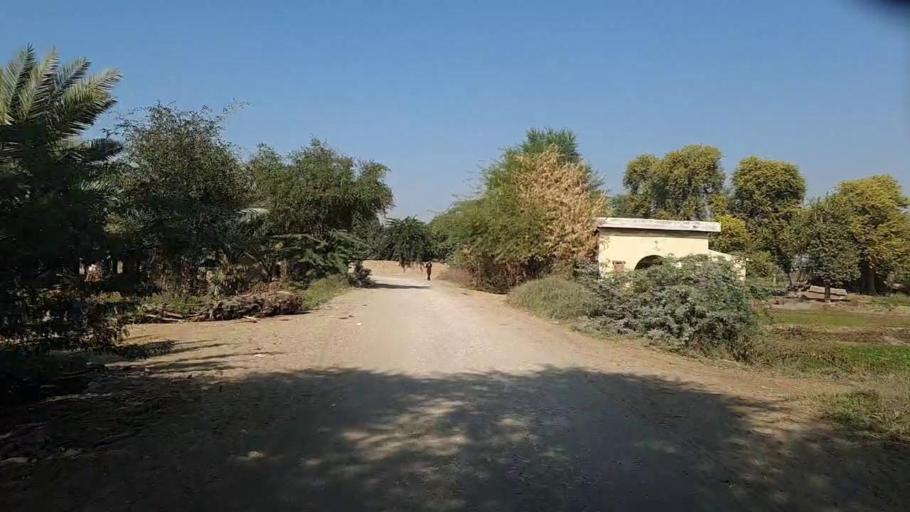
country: PK
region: Sindh
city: Bozdar
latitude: 27.1936
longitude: 68.6686
